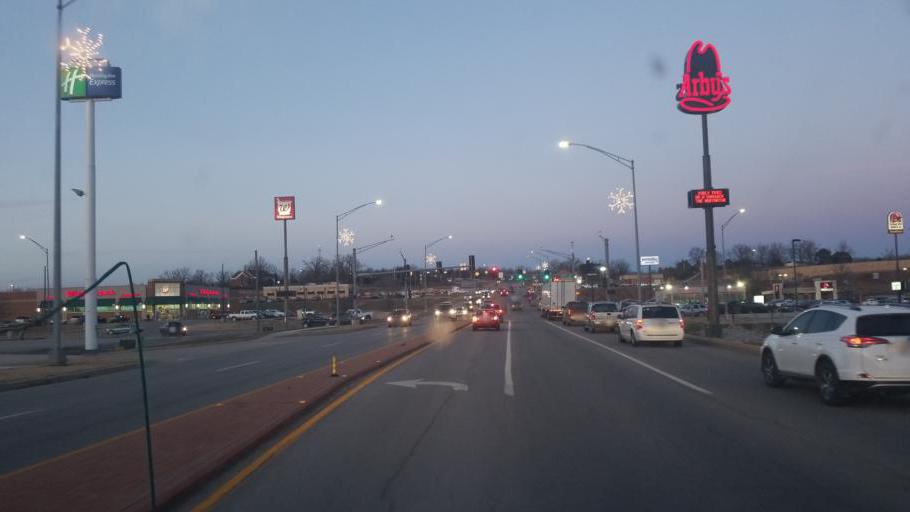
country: US
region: Missouri
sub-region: Howell County
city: West Plains
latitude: 36.7154
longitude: -91.8739
